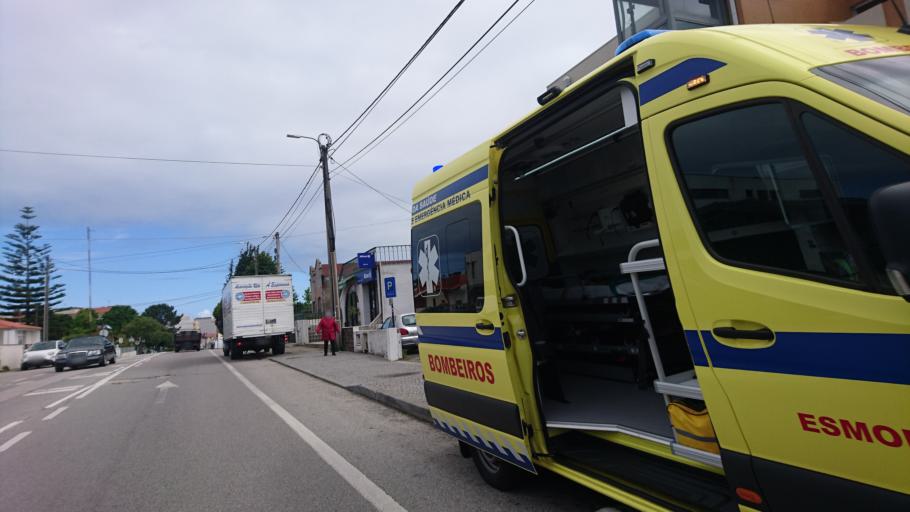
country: PT
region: Aveiro
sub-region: Ovar
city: Esmoriz
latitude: 40.9537
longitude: -8.6252
